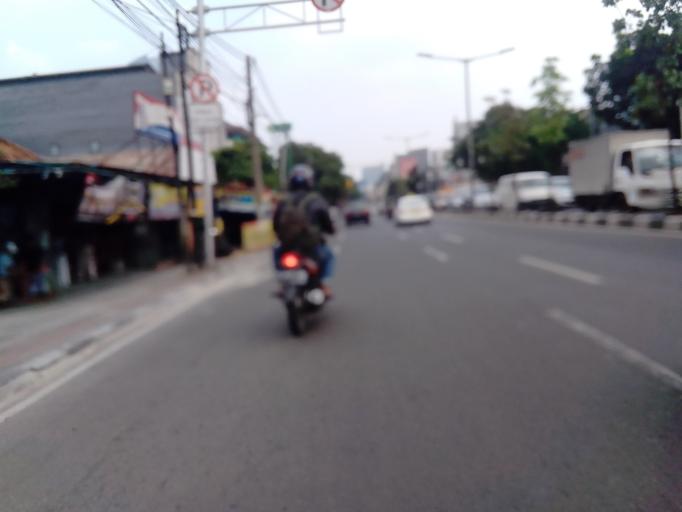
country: ID
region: Jakarta Raya
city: Jakarta
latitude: -6.1958
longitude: 106.8145
